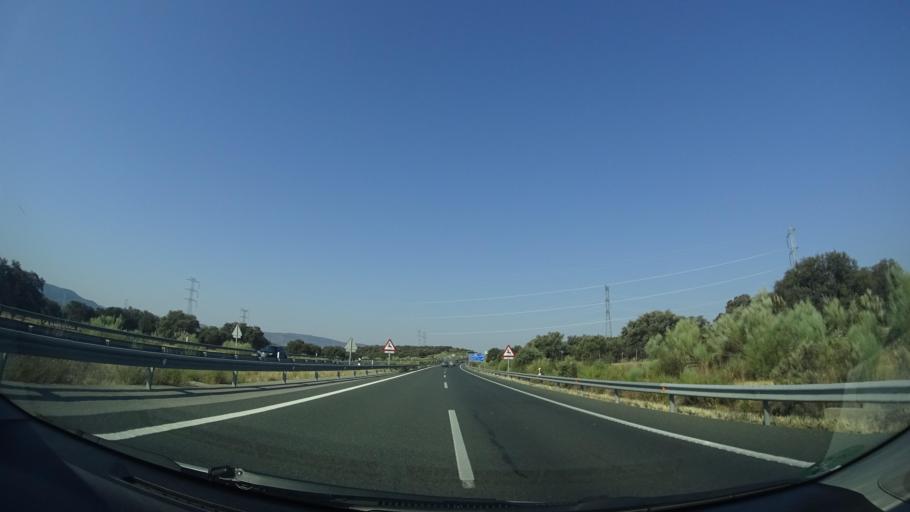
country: ES
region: Extremadura
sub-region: Provincia de Caceres
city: Almaraz
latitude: 39.7941
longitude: -5.6859
